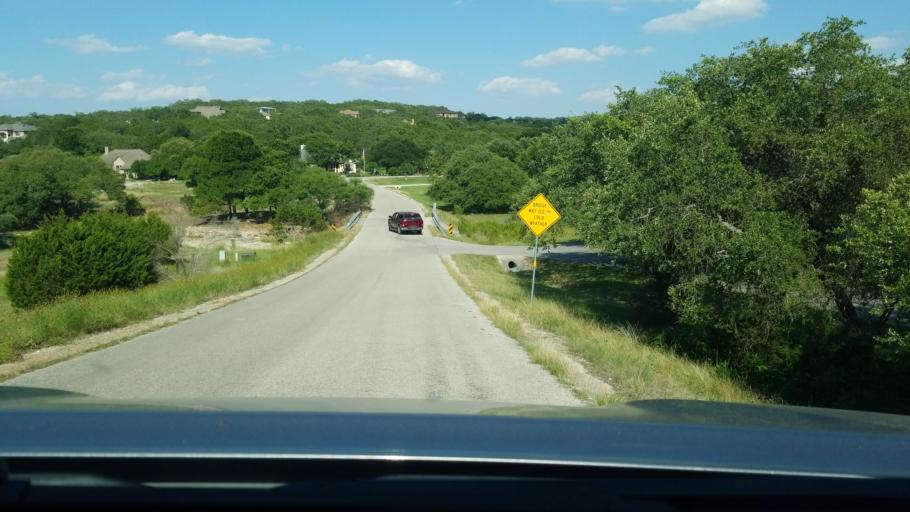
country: US
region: Texas
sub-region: Comal County
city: Bulverde
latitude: 29.8252
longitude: -98.4018
